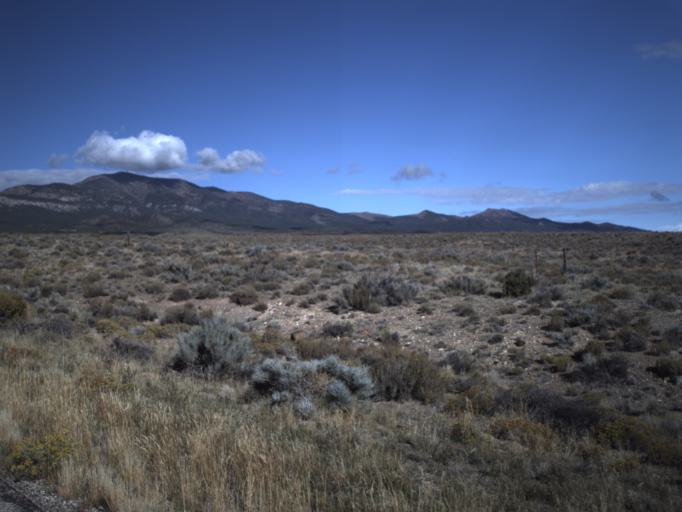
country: US
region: Utah
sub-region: Beaver County
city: Milford
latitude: 38.4504
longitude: -113.1982
